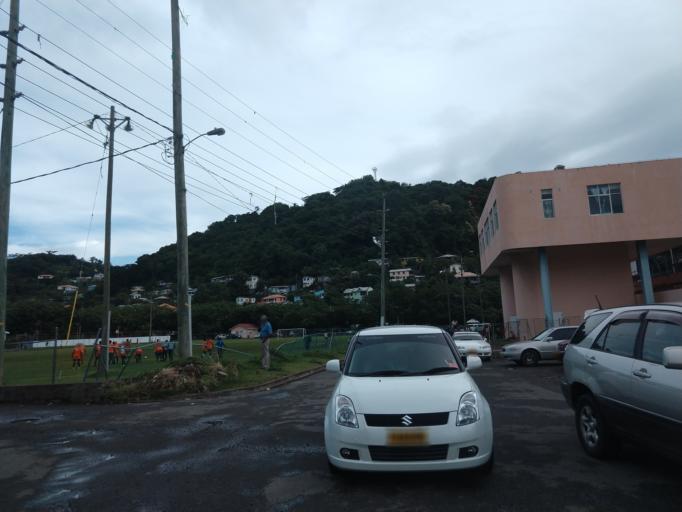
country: GD
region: Saint George
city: Saint George's
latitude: 12.0596
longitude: -61.7512
